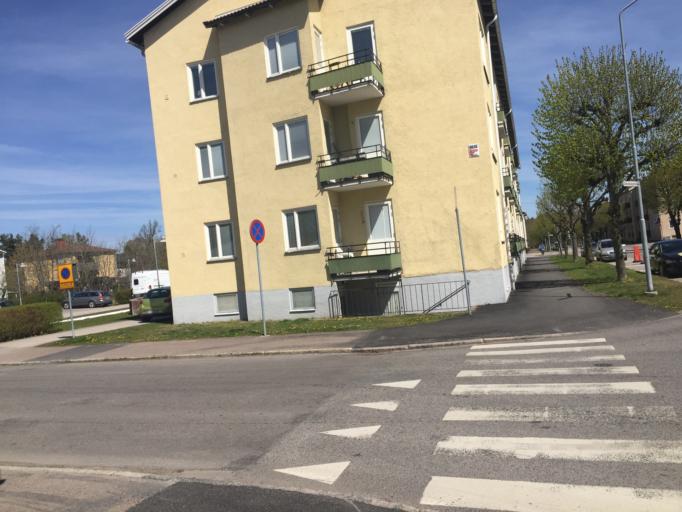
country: SE
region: Kalmar
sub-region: Nybro Kommun
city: Nybro
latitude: 56.7454
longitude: 15.8986
